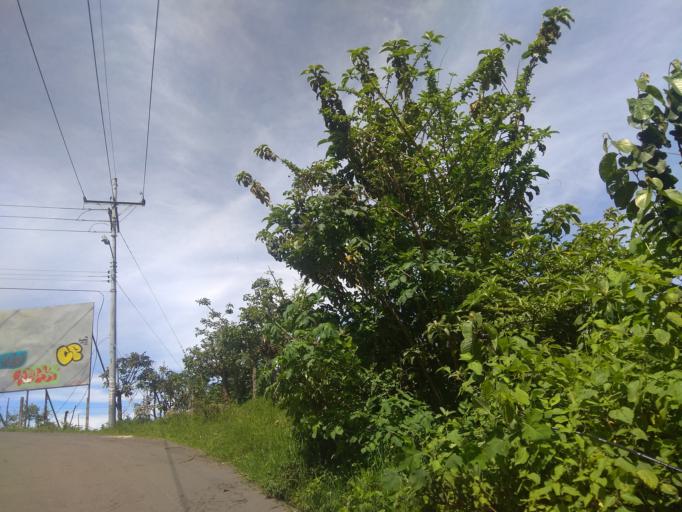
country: CR
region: Cartago
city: Cot
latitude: 9.9217
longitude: -83.9007
